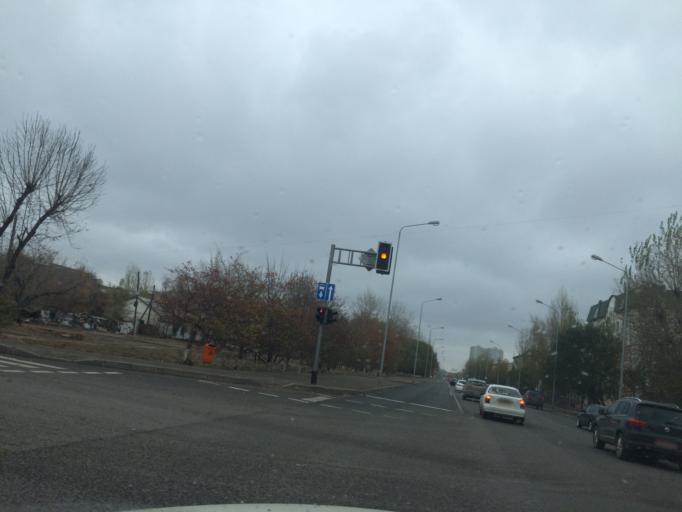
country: KZ
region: Astana Qalasy
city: Astana
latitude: 51.1701
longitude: 71.4505
